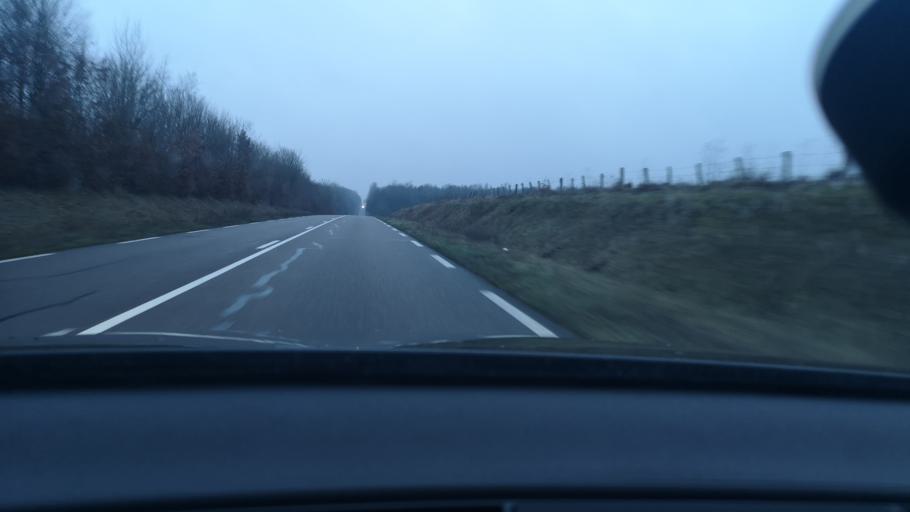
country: FR
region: Bourgogne
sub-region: Departement de la Cote-d'Or
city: Aiserey
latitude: 47.1156
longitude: 5.1004
